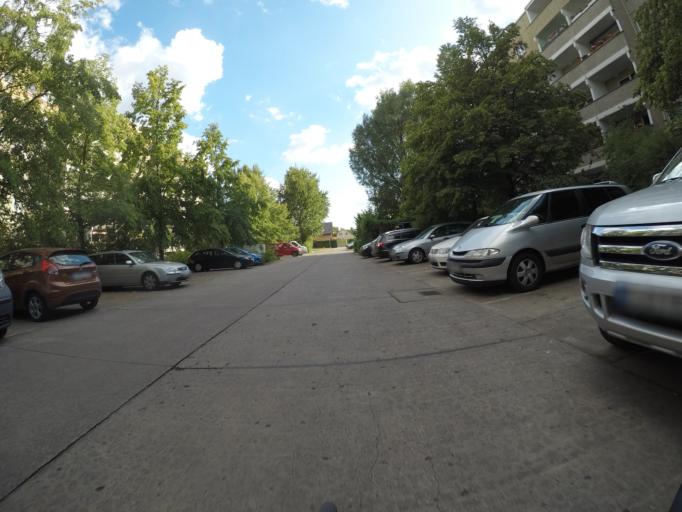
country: DE
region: Berlin
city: Hellersdorf
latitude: 52.5285
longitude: 13.6195
